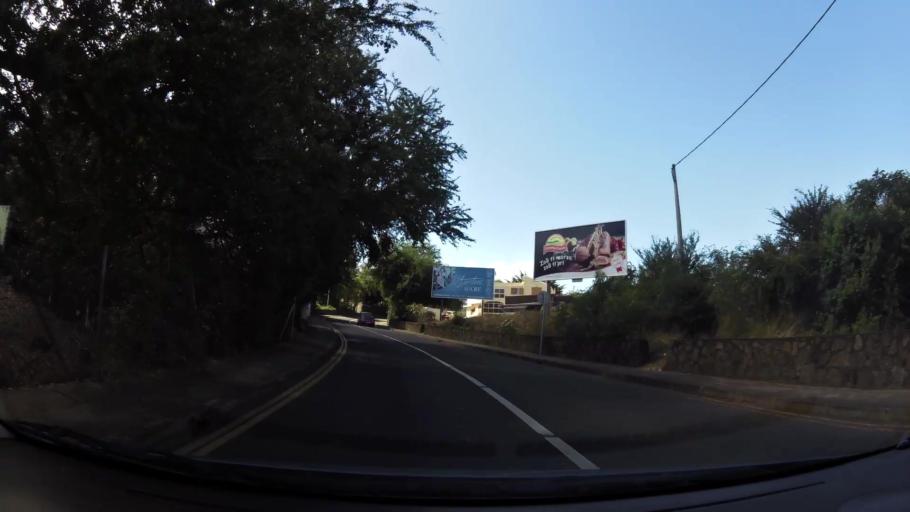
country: MU
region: Black River
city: Flic en Flac
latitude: -20.2766
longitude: 57.3744
